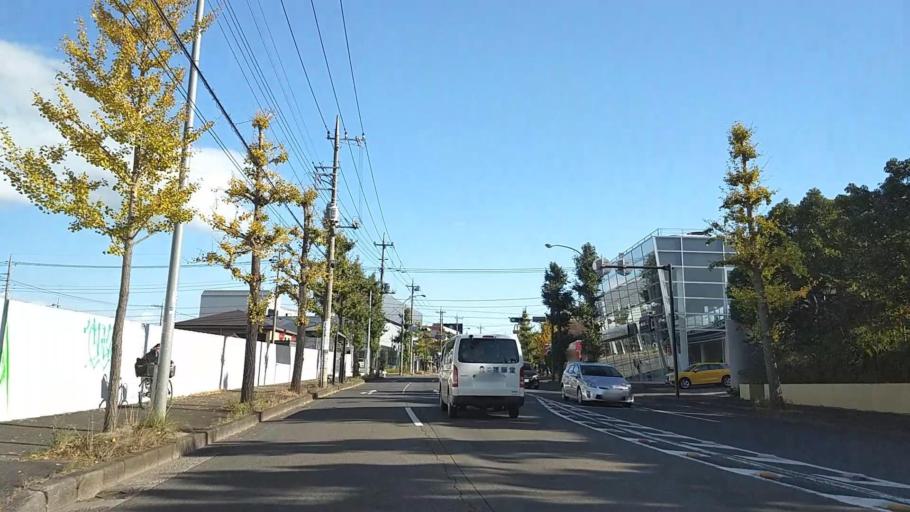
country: JP
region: Tokyo
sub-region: Machida-shi
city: Machida
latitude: 35.5439
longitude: 139.5490
